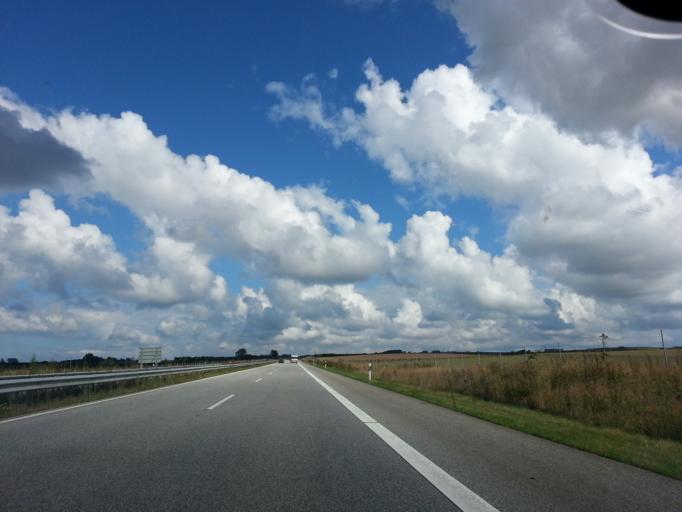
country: DE
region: Schleswig-Holstein
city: Gremersdorf
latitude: 54.3432
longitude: 10.9448
